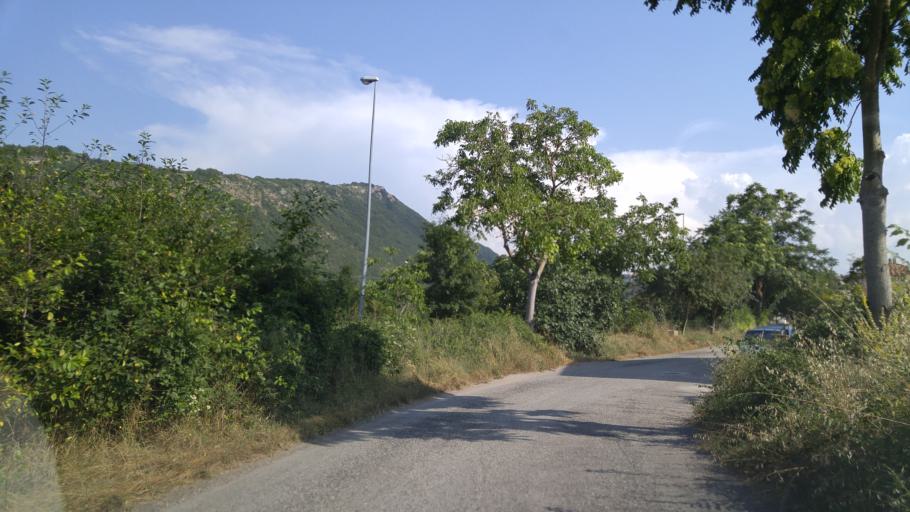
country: IT
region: The Marches
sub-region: Provincia di Pesaro e Urbino
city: Acqualagna
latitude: 43.6145
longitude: 12.6717
